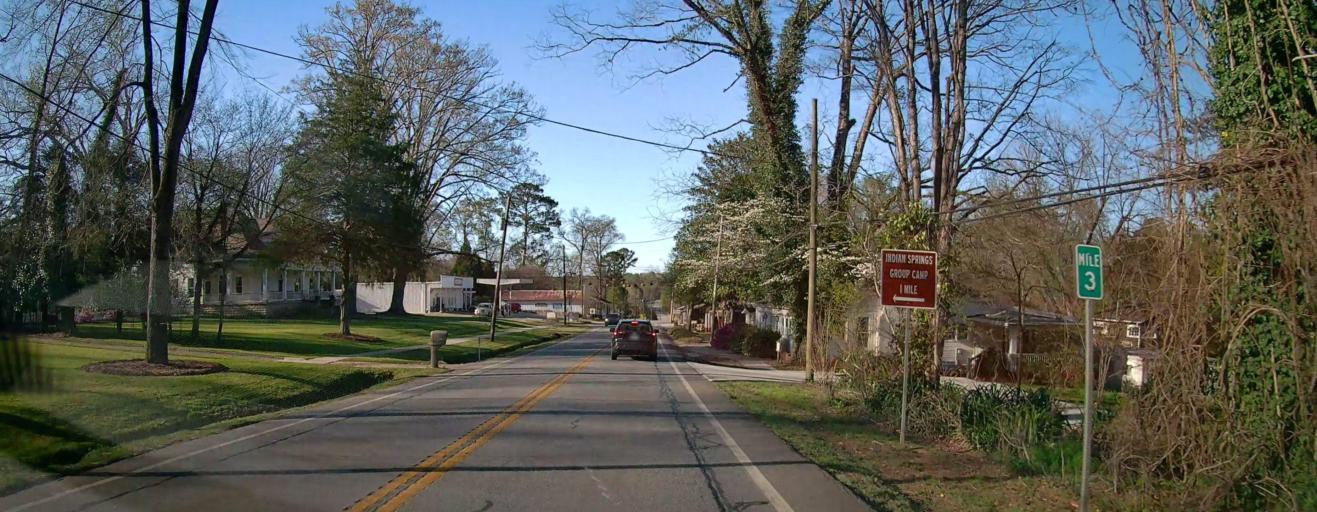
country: US
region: Georgia
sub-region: Butts County
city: Indian Springs
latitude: 33.2420
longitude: -83.9208
